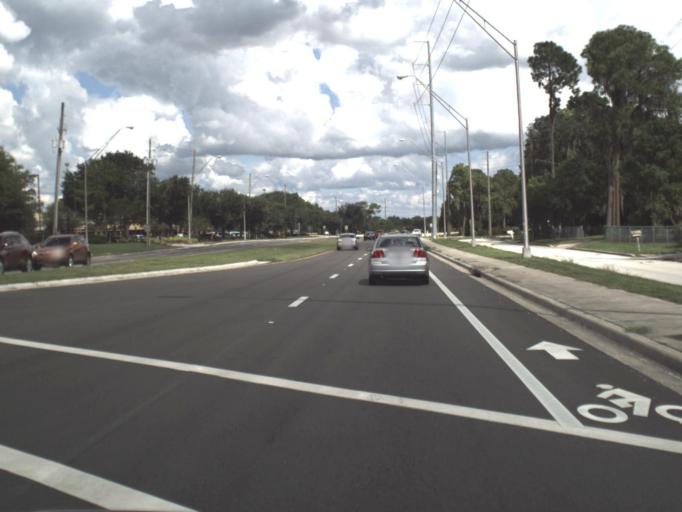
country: US
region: Florida
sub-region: Polk County
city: Jan-Phyl Village
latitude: 28.0048
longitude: -81.7794
